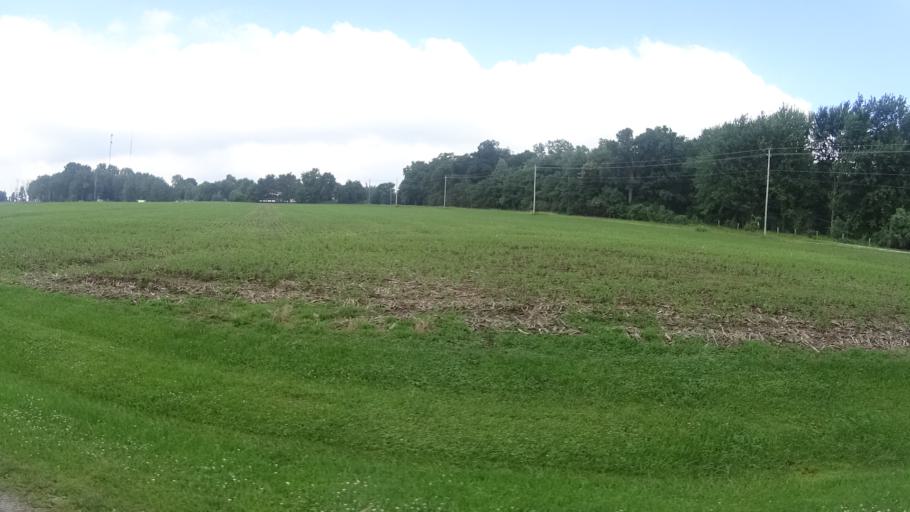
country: US
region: Ohio
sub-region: Huron County
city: Wakeman
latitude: 41.3113
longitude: -82.4432
